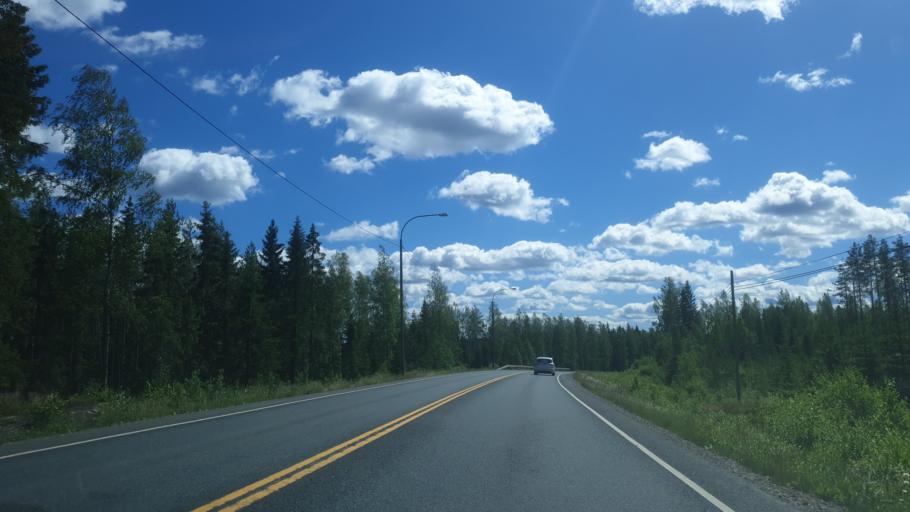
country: FI
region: Northern Savo
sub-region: Varkaus
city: Leppaevirta
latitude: 62.5670
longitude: 27.6160
